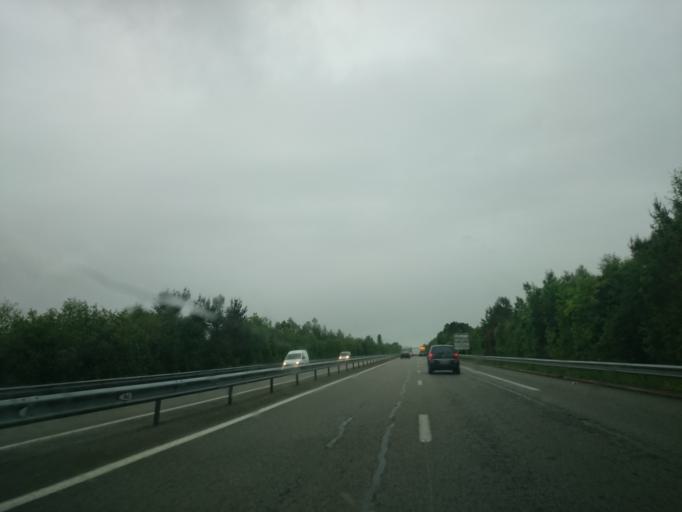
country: FR
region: Brittany
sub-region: Departement du Morbihan
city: Guer
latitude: 47.9445
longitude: -2.1017
